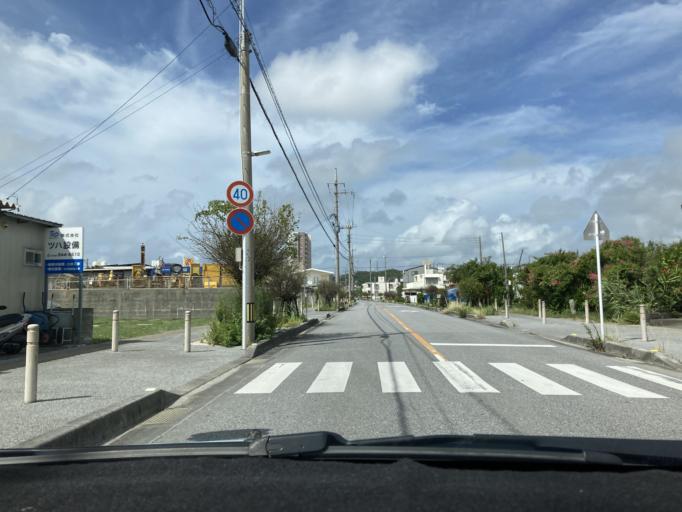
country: JP
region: Okinawa
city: Ginowan
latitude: 26.2233
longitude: 127.7701
